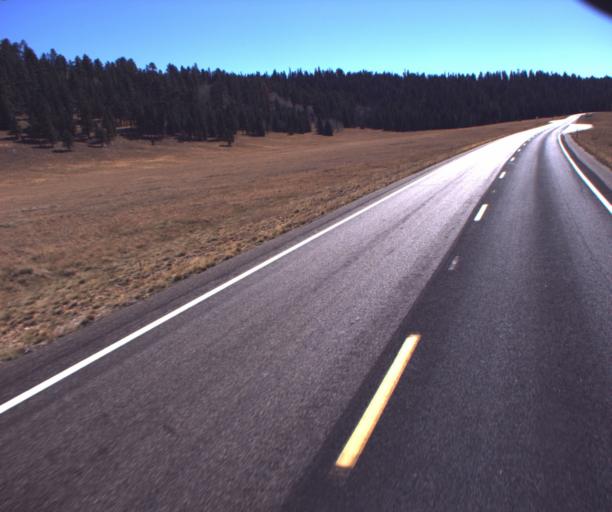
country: US
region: Arizona
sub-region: Coconino County
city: Grand Canyon
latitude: 36.4774
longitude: -112.1261
